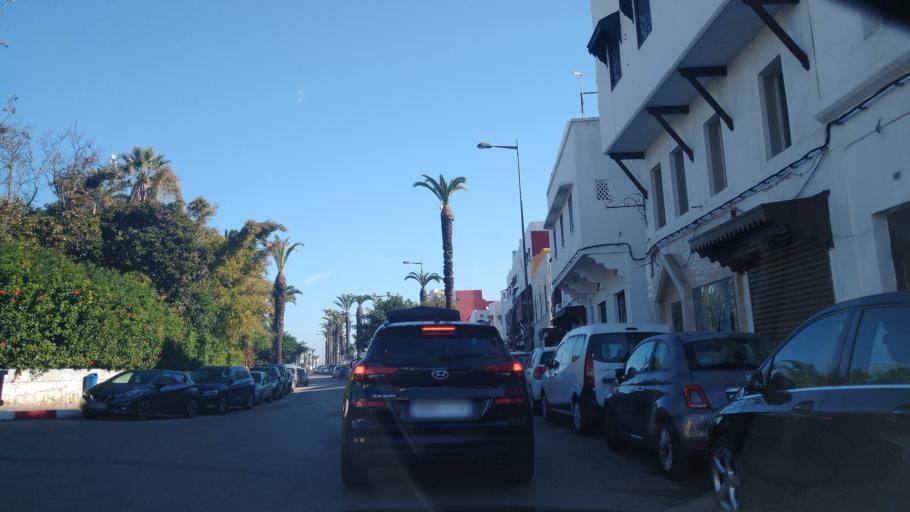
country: MA
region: Rabat-Sale-Zemmour-Zaer
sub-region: Rabat
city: Rabat
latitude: 34.0273
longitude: -6.8409
